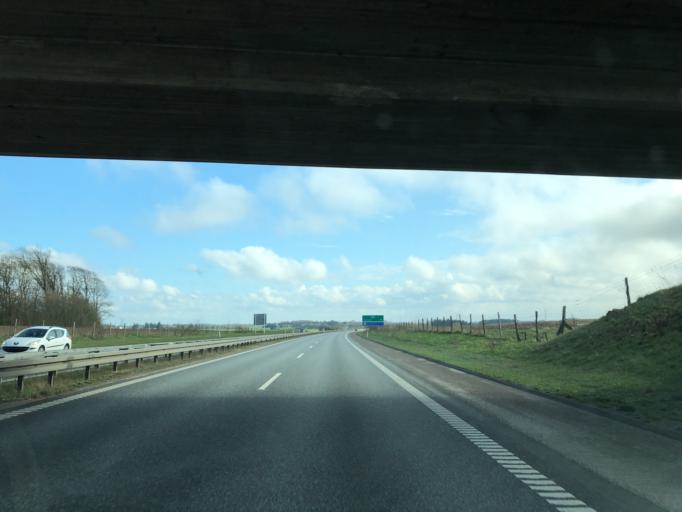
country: DK
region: North Denmark
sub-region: Hjorring Kommune
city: Vra
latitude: 57.3551
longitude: 10.0299
